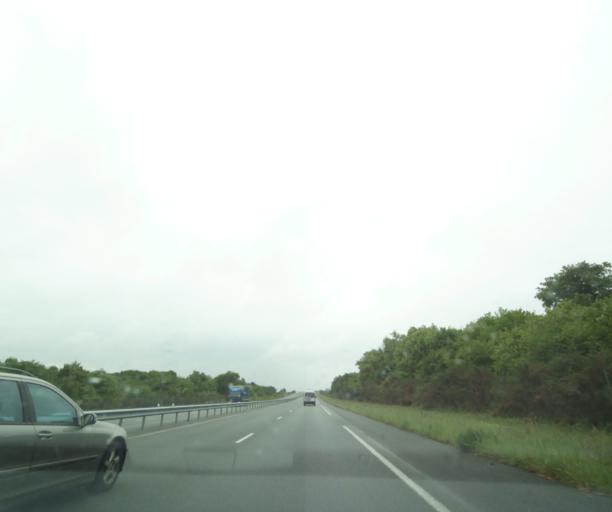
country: FR
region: Poitou-Charentes
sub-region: Departement de la Charente-Maritime
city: Nieul-les-Saintes
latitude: 45.7017
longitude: -0.7542
